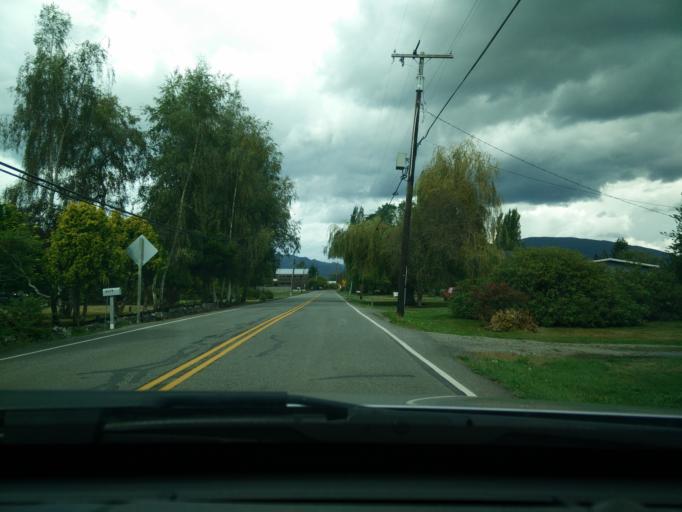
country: US
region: Washington
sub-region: Skagit County
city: Burlington
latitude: 48.5590
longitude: -122.4443
